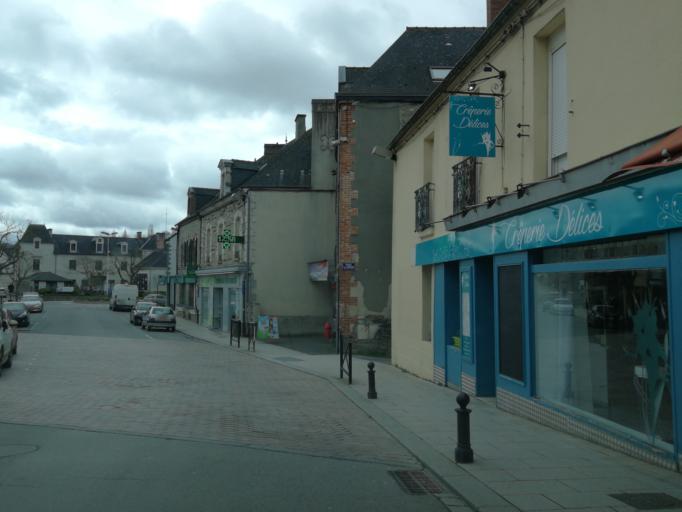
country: FR
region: Brittany
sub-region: Departement d'Ille-et-Vilaine
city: Guichen
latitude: 47.9673
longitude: -1.7964
